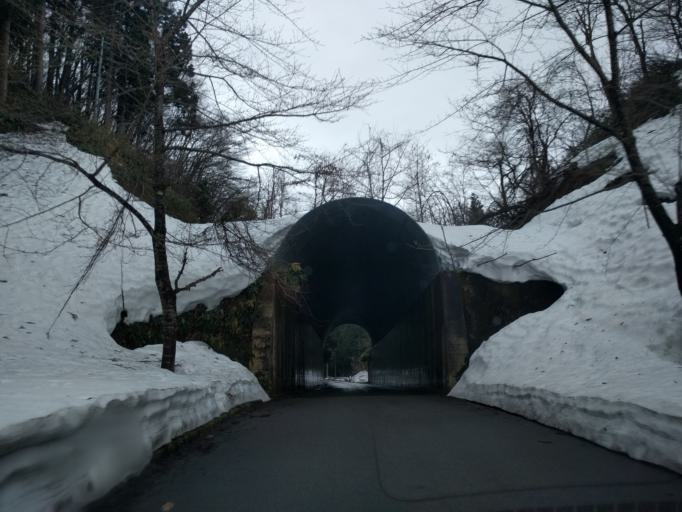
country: JP
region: Fukushima
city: Kitakata
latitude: 37.6923
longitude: 139.9457
